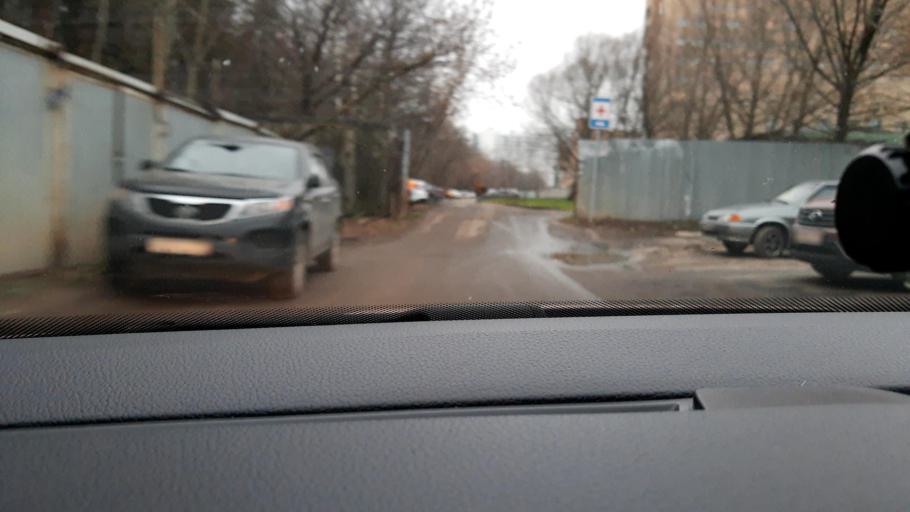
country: RU
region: Moskovskaya
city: Koptevo
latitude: 55.8174
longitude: 37.5375
